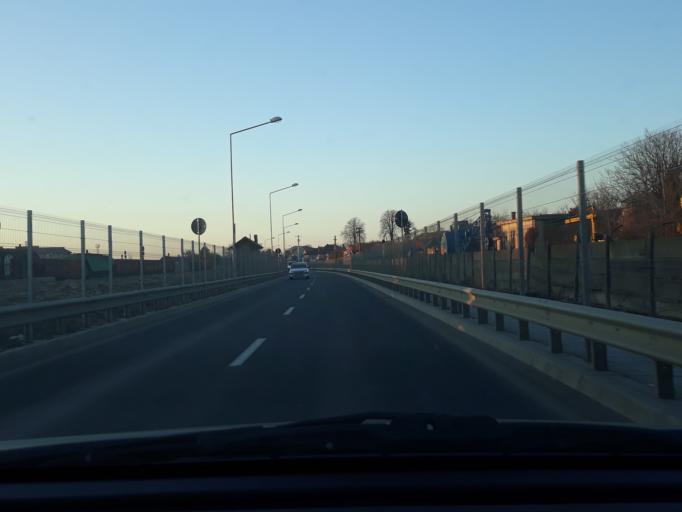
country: RO
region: Bihor
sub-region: Comuna Biharea
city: Oradea
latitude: 47.0746
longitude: 21.9342
